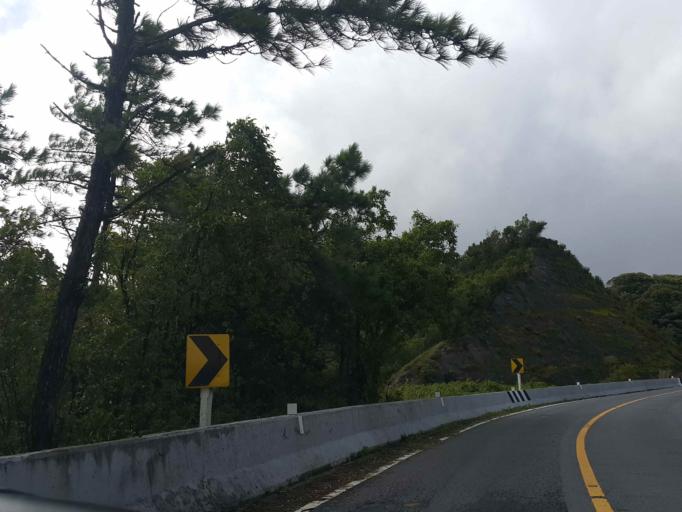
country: TH
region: Chiang Mai
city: Mae Chaem
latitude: 18.5465
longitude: 98.4848
